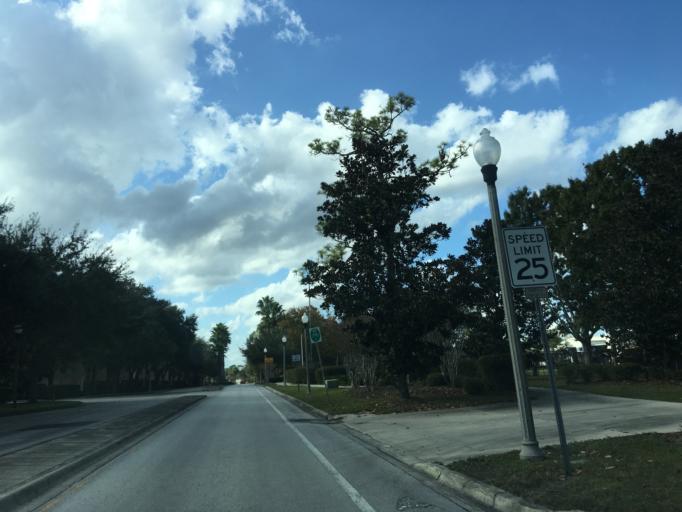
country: US
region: Florida
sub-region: Orange County
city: Eatonville
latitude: 28.6275
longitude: -81.3988
